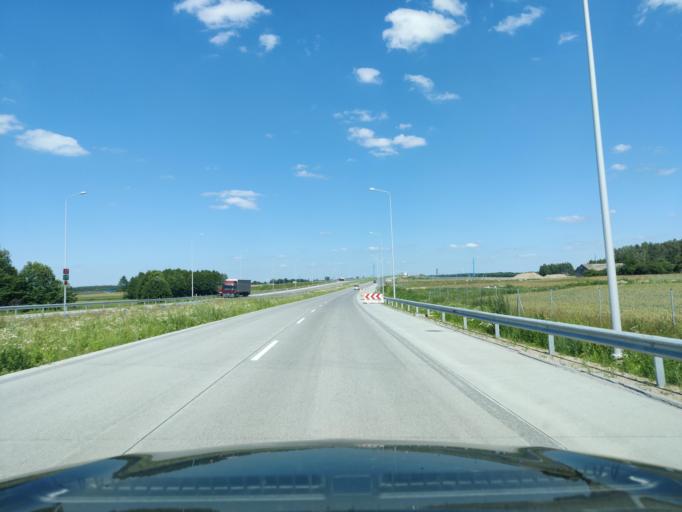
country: PL
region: Masovian Voivodeship
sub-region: Powiat mlawski
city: Wisniewo
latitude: 53.0696
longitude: 20.3715
